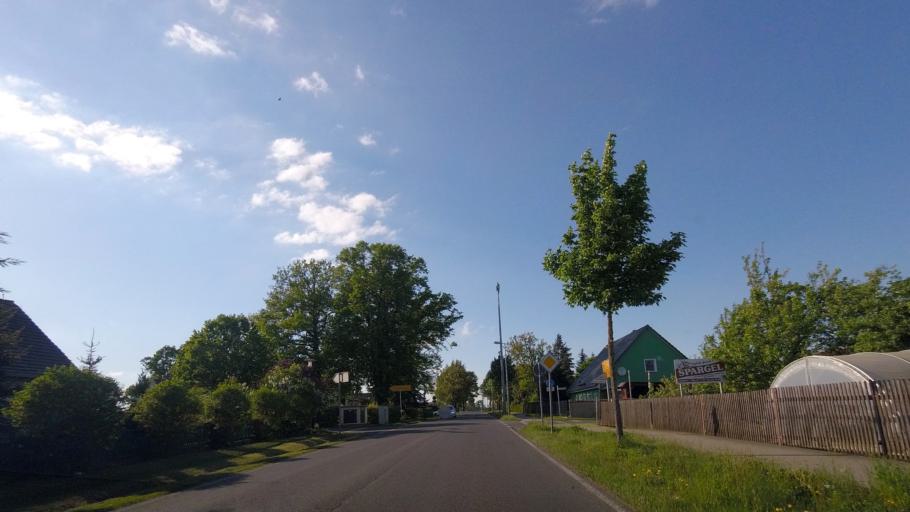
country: DE
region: Brandenburg
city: Lubbenau
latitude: 51.8687
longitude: 13.9179
